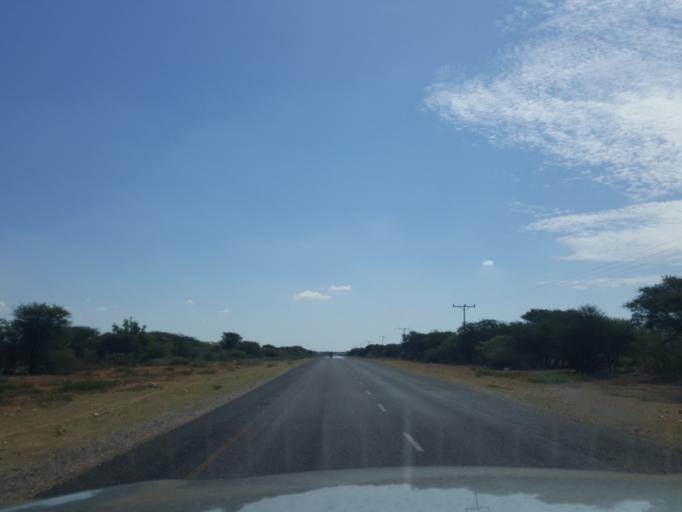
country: BW
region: Kweneng
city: Letlhakeng
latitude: -24.1199
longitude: 25.0693
